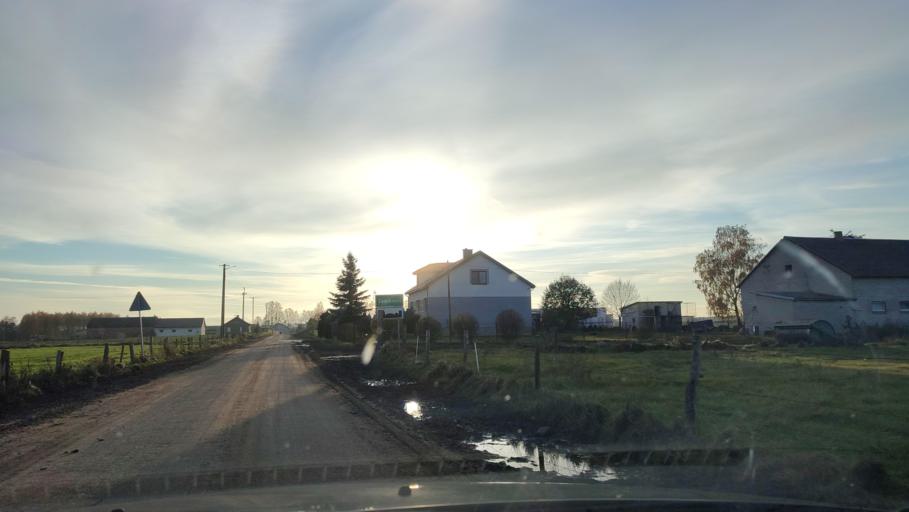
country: PL
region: Masovian Voivodeship
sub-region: Powiat mlawski
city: Dzierzgowo
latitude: 53.2827
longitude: 20.6527
